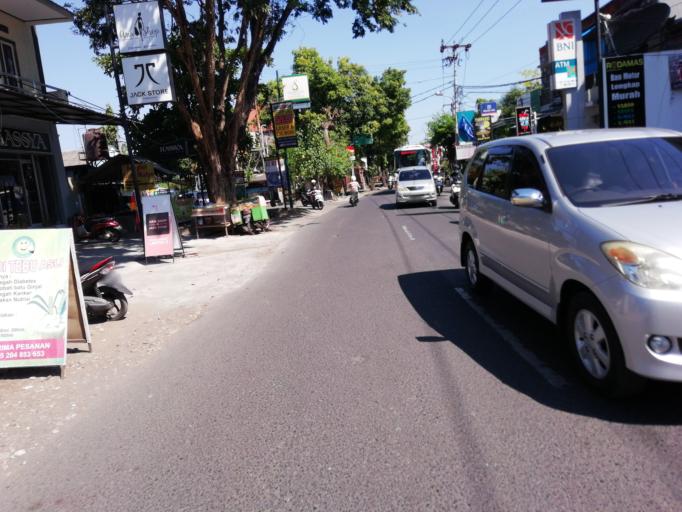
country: ID
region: Bali
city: Karyadharma
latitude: -8.6834
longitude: 115.2263
